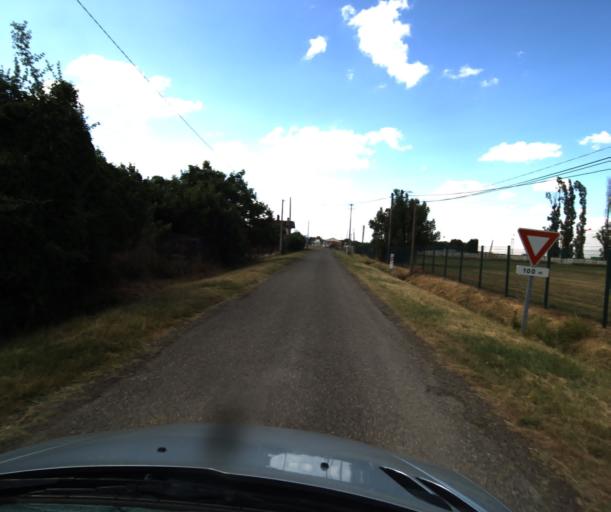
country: FR
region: Midi-Pyrenees
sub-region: Departement du Tarn-et-Garonne
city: Finhan
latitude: 43.9235
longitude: 1.2638
